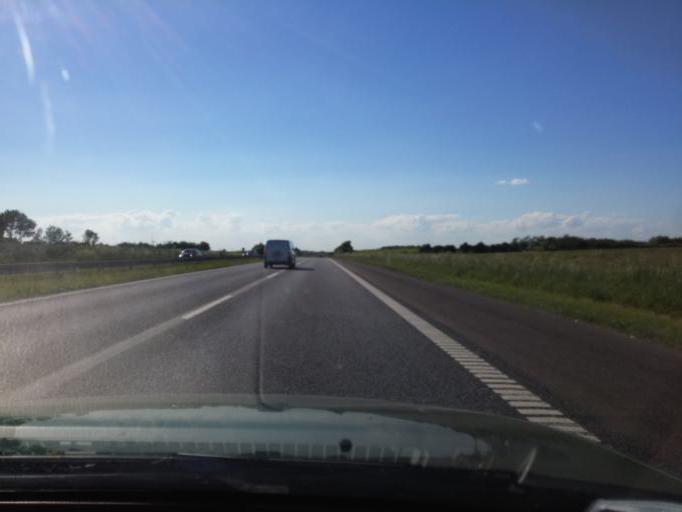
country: DK
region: South Denmark
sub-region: Middelfart Kommune
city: Ejby
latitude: 55.4563
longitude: 9.9386
